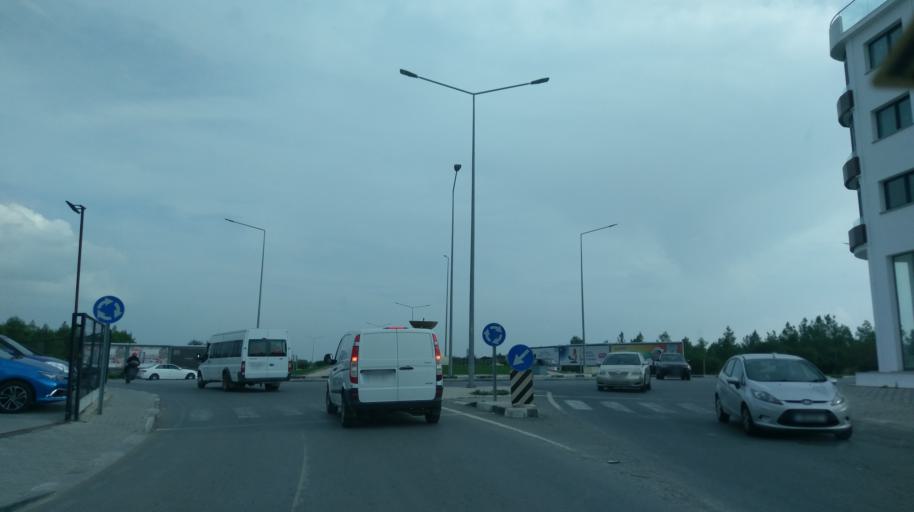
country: CY
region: Lefkosia
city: Nicosia
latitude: 35.1910
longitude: 33.3268
